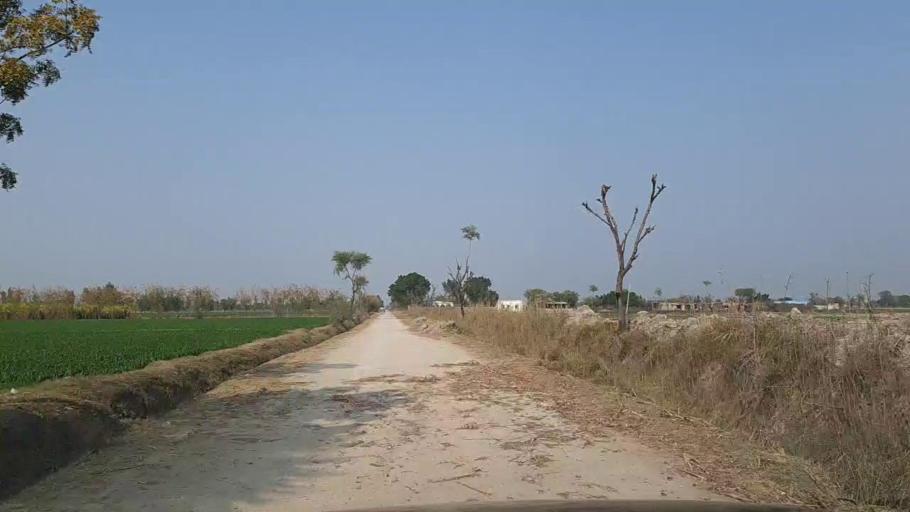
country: PK
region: Sindh
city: Daur
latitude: 26.3961
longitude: 68.4238
